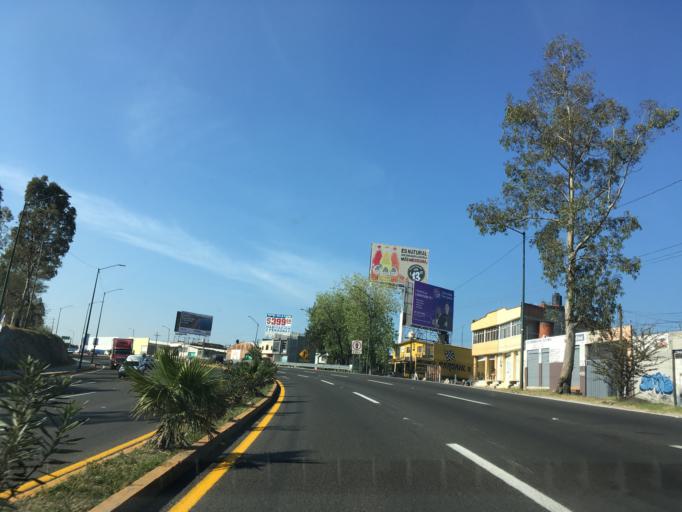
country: MX
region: Michoacan
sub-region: Tarimbaro
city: Fraccionamiento Privadas del Sol
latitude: 19.7370
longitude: -101.1817
